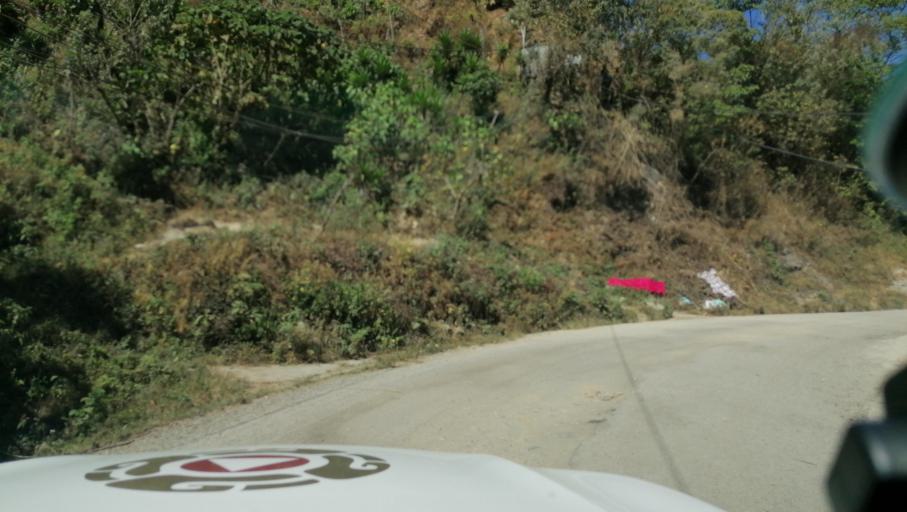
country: GT
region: San Marcos
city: Tacana
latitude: 15.1930
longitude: -92.1869
